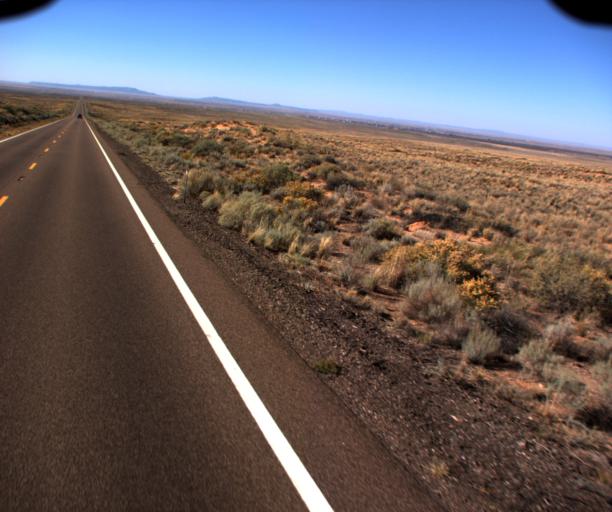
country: US
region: Arizona
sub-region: Navajo County
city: Winslow
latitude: 35.0623
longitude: -110.5825
